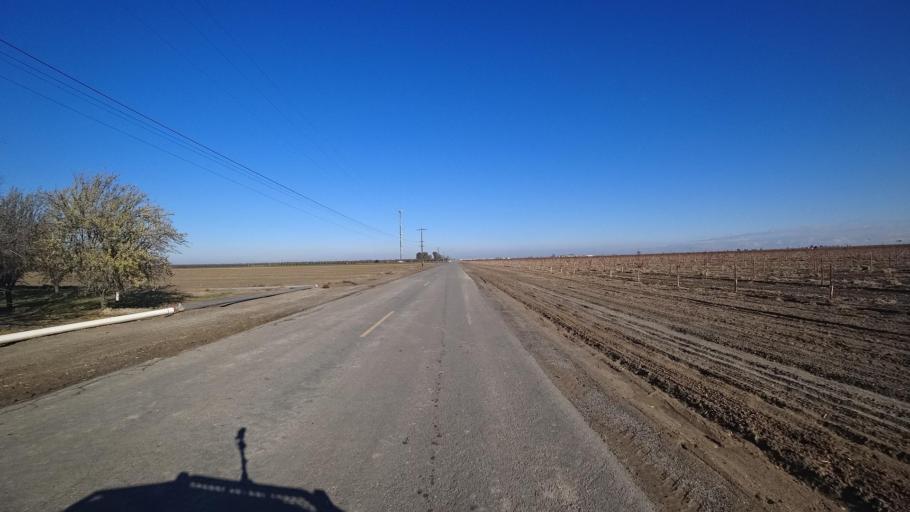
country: US
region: California
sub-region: Kern County
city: Delano
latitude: 35.7478
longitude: -119.3119
